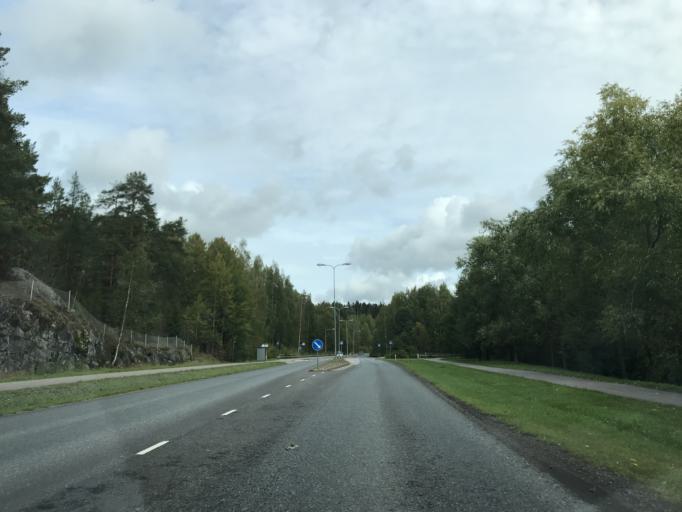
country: FI
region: Paijanne Tavastia
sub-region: Lahti
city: Lahti
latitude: 60.9946
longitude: 25.7484
